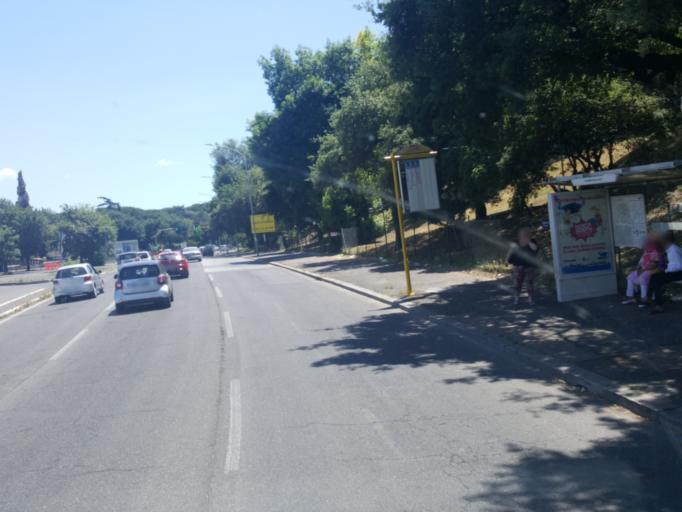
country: IT
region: Latium
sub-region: Citta metropolitana di Roma Capitale
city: Selcetta
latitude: 41.8242
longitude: 12.4643
